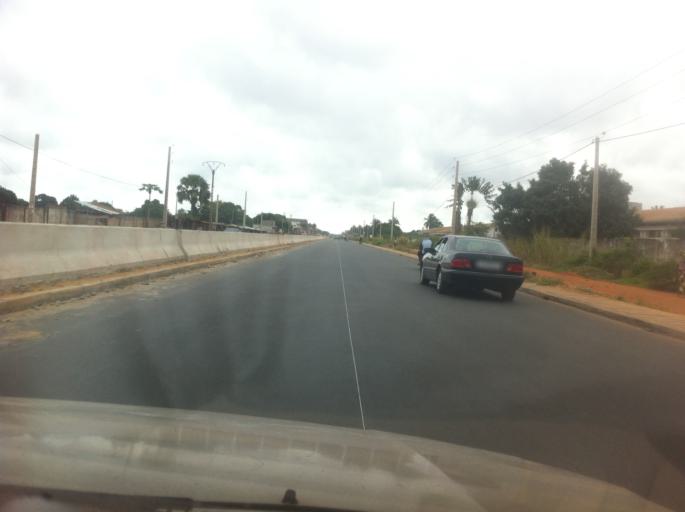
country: BJ
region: Atlantique
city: Ouidah
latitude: 6.3737
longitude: 2.0789
